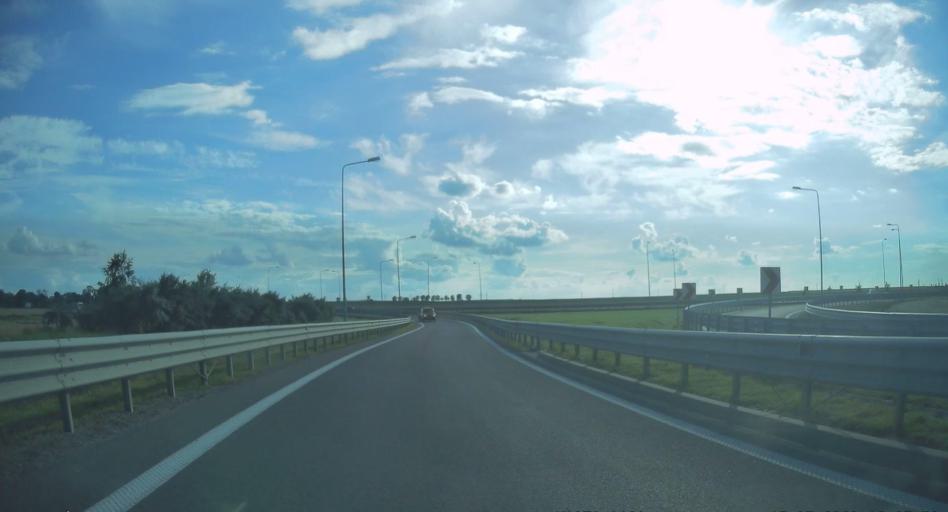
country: PL
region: Subcarpathian Voivodeship
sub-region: Powiat przemyski
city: Orly
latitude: 49.9060
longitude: 22.8187
